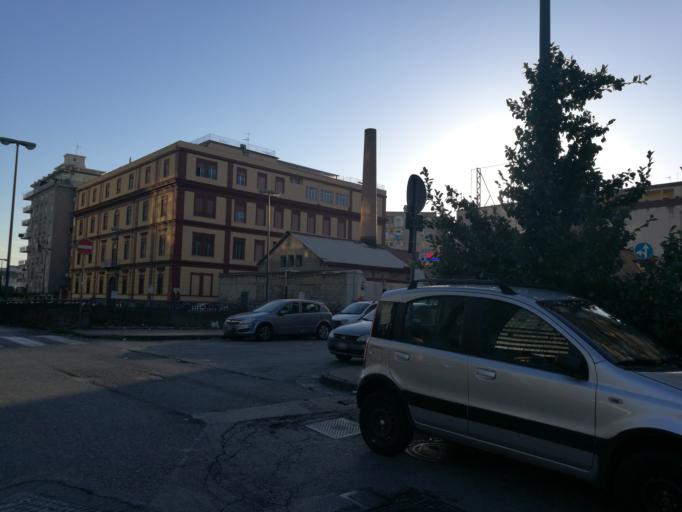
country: IT
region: Campania
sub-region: Provincia di Napoli
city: Napoli
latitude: 40.8582
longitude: 14.2768
